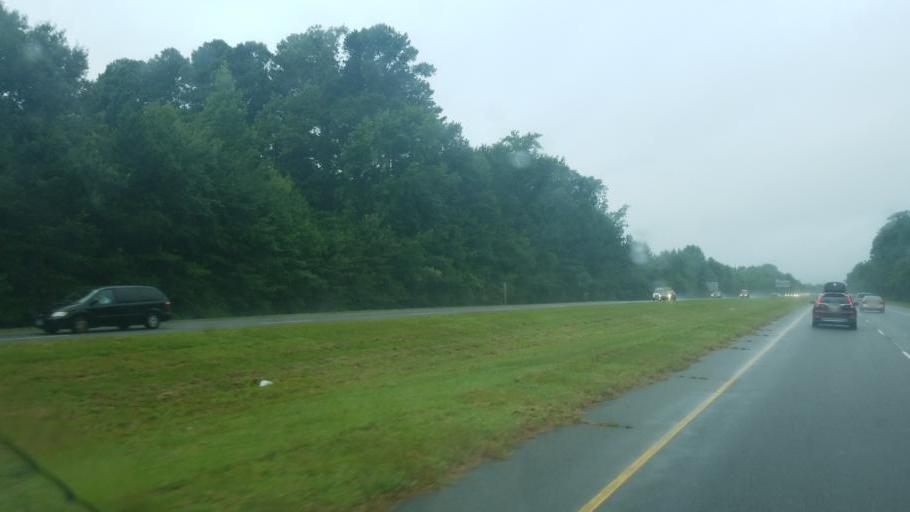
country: US
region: Virginia
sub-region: City of Chesapeake
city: Chesapeake
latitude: 36.7398
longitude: -76.2487
